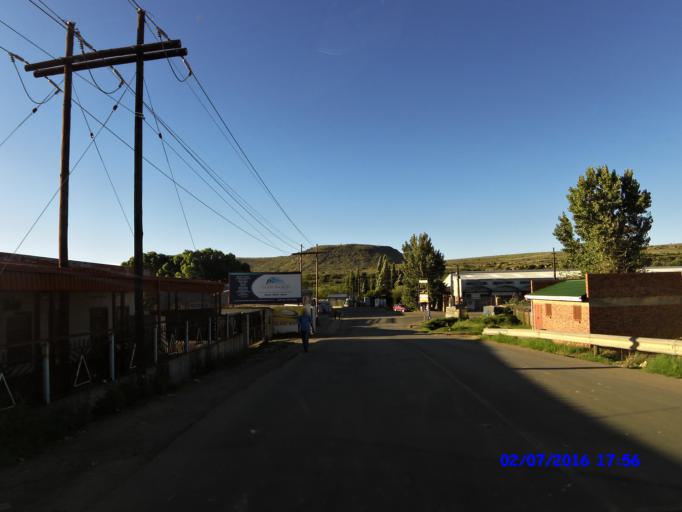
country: LS
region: Maseru
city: Maseru
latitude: -29.2972
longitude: 27.4732
